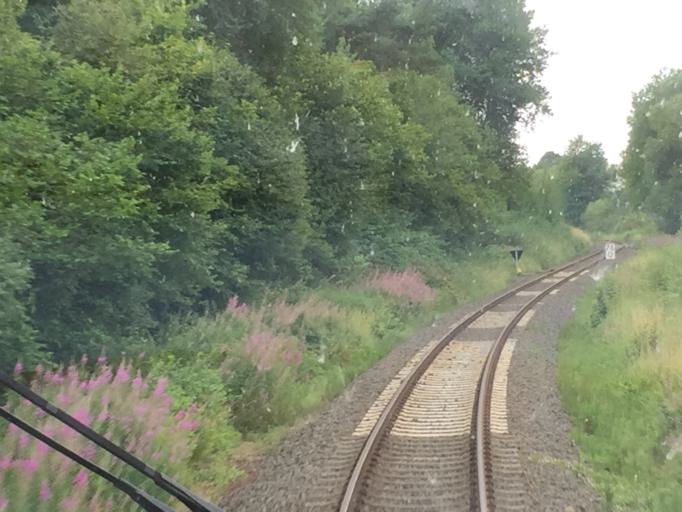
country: DE
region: Hesse
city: Frankenberg
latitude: 51.0487
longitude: 8.7800
